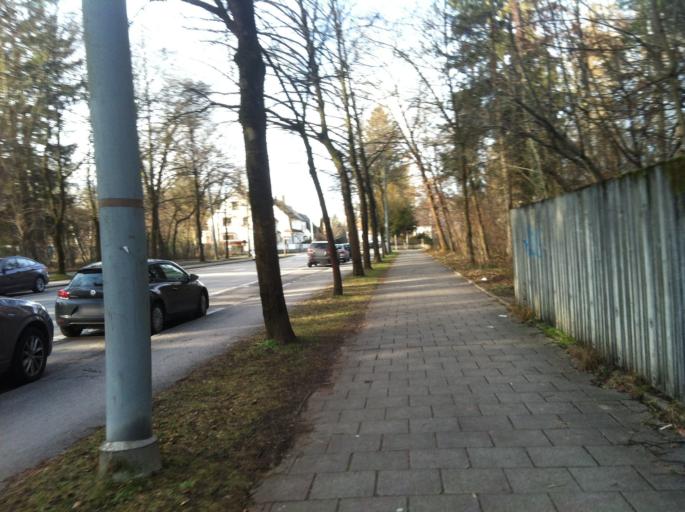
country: DE
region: Bavaria
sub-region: Upper Bavaria
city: Pullach im Isartal
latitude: 48.0906
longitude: 11.5247
